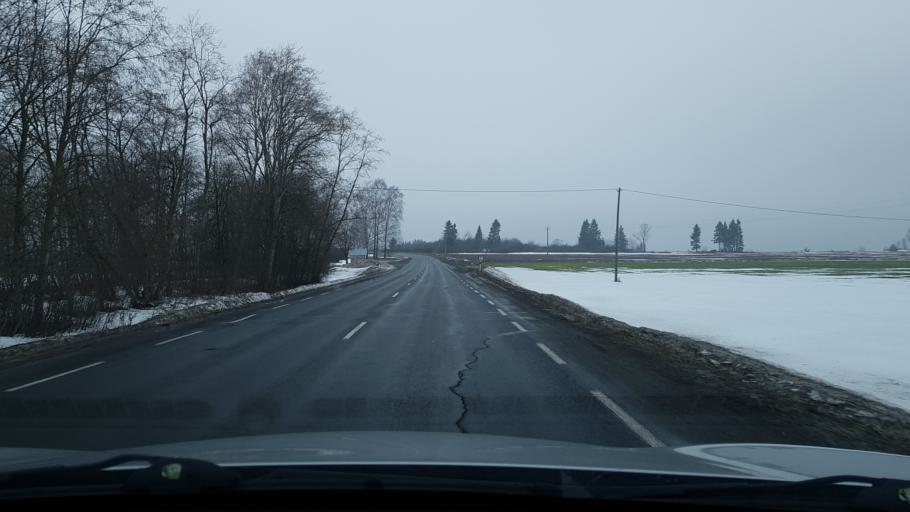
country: EE
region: Viljandimaa
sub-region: Viiratsi vald
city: Viiratsi
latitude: 58.2505
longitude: 25.8382
